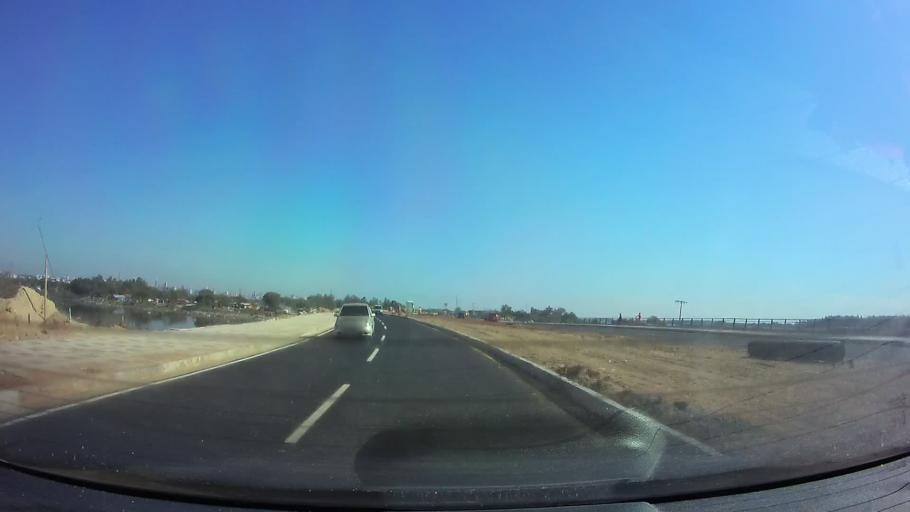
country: PY
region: Asuncion
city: Asuncion
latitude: -25.2470
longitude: -57.5977
